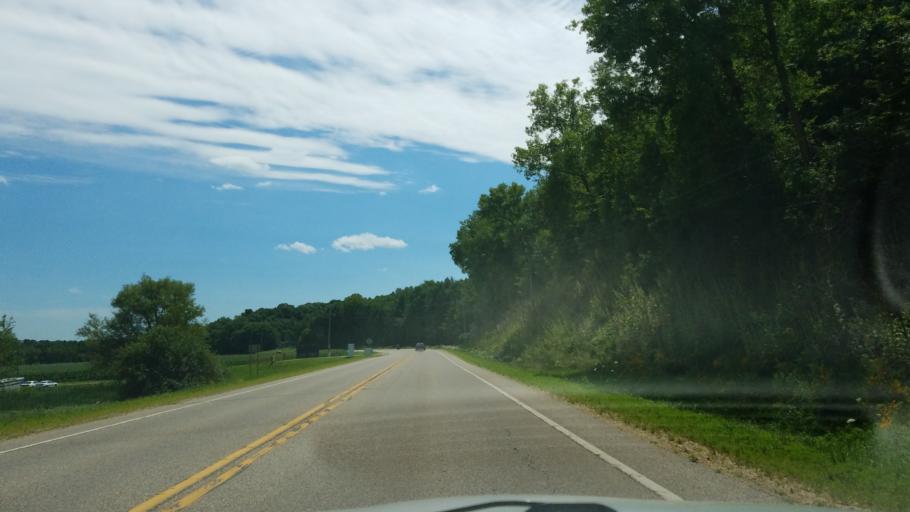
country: US
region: Wisconsin
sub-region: Saint Croix County
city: Glenwood City
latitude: 45.0530
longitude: -92.1774
